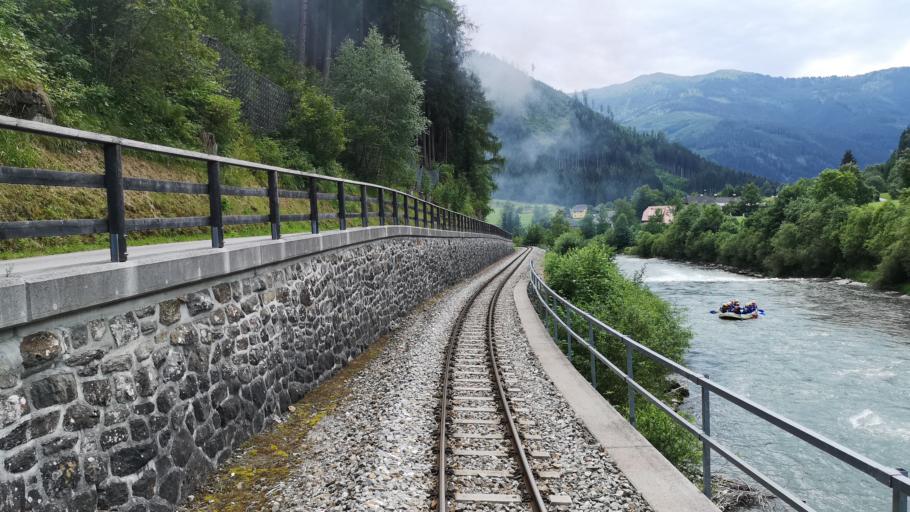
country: AT
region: Salzburg
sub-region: Politischer Bezirk Tamsweg
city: Ramingstein
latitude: 47.0802
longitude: 13.8147
